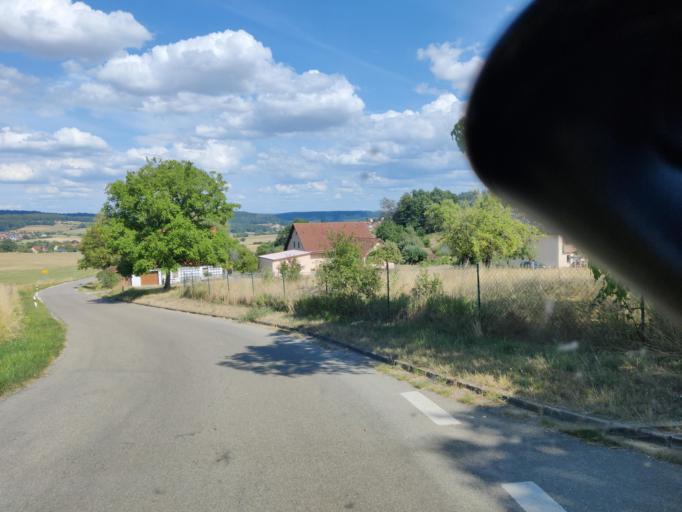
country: DE
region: Bavaria
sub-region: Regierungsbezirk Mittelfranken
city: Thalmassing
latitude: 49.0749
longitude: 11.2297
